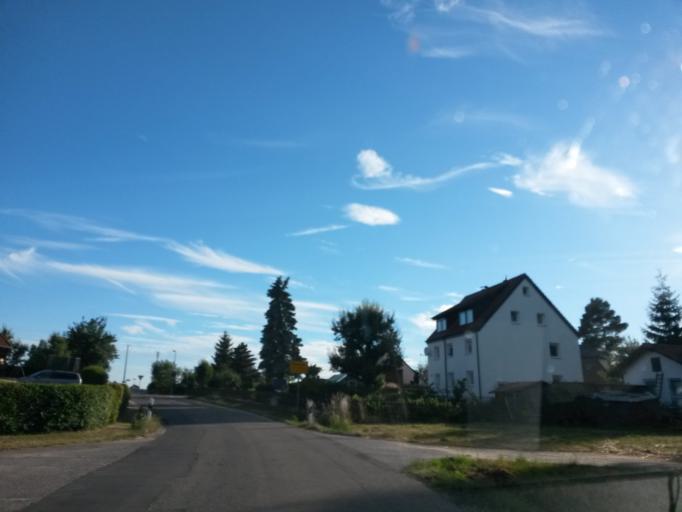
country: DE
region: Baden-Wuerttemberg
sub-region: Regierungsbezirk Stuttgart
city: Ellenberg
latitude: 49.0757
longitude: 10.2080
